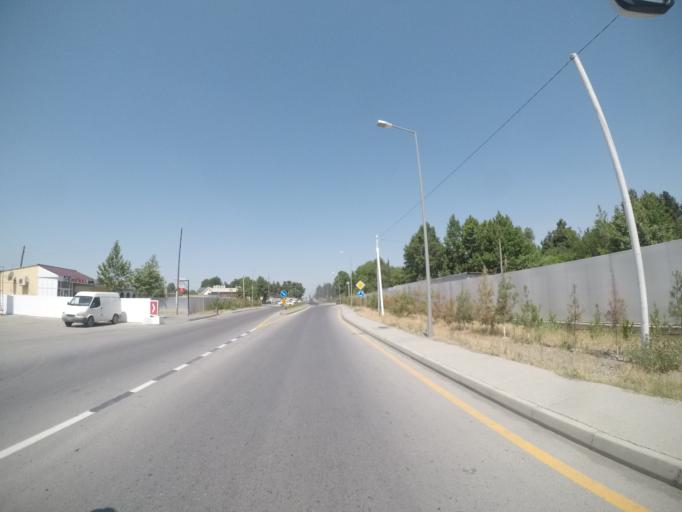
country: AZ
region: Agdas
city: Agdas
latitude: 40.6300
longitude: 47.4663
